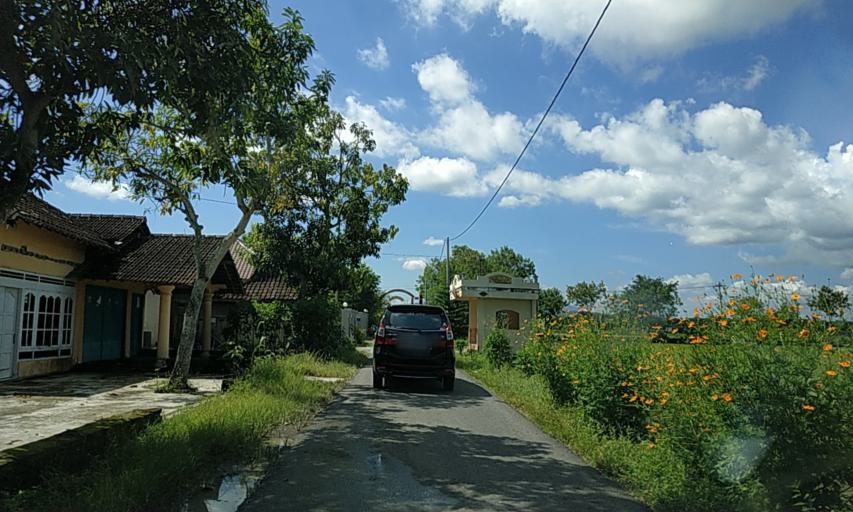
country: ID
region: Central Java
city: Trucuk
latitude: -7.7460
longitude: 110.7374
